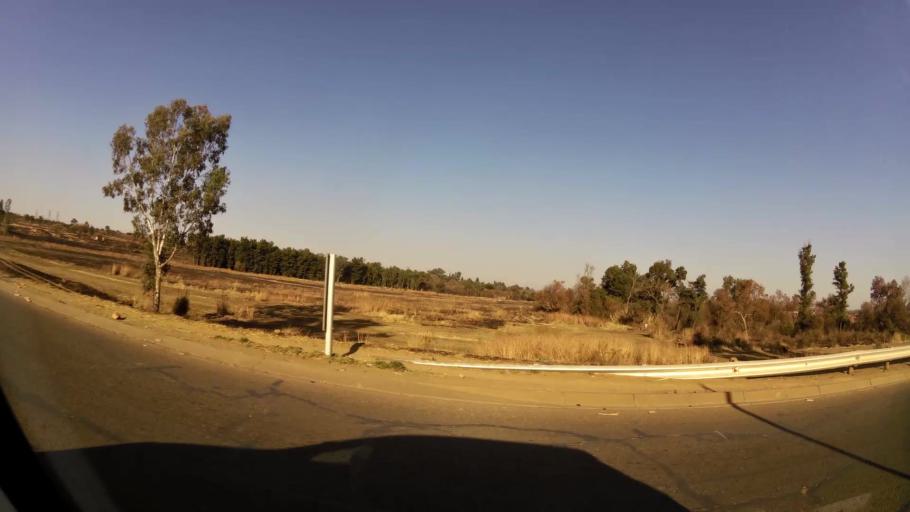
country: ZA
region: Gauteng
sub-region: City of Tshwane Metropolitan Municipality
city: Cullinan
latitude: -25.7453
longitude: 28.3727
